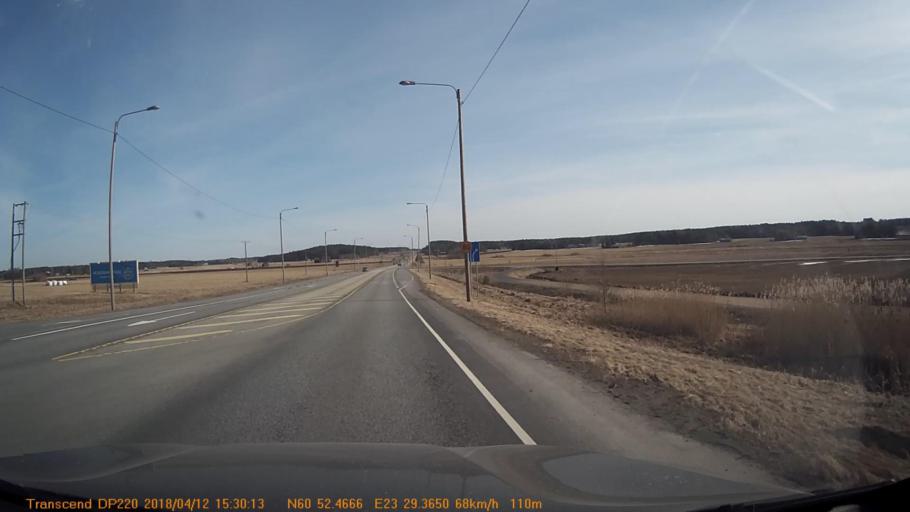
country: FI
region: Haeme
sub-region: Forssa
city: Jokioinen
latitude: 60.8738
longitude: 23.4904
